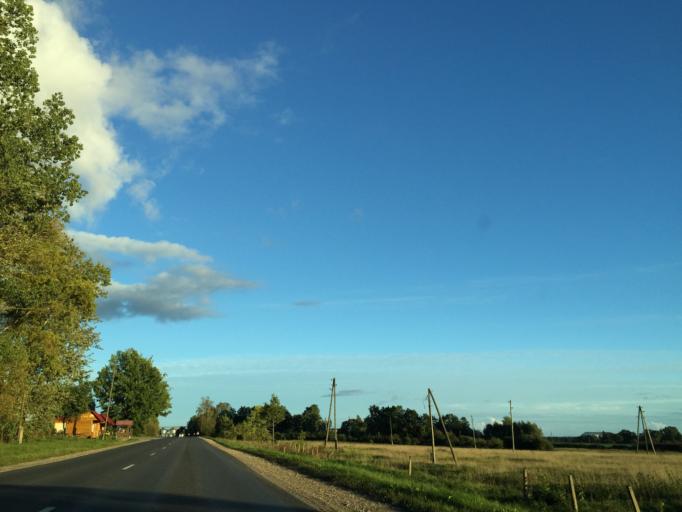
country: LV
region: Saldus Rajons
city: Saldus
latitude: 56.6918
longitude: 22.4484
